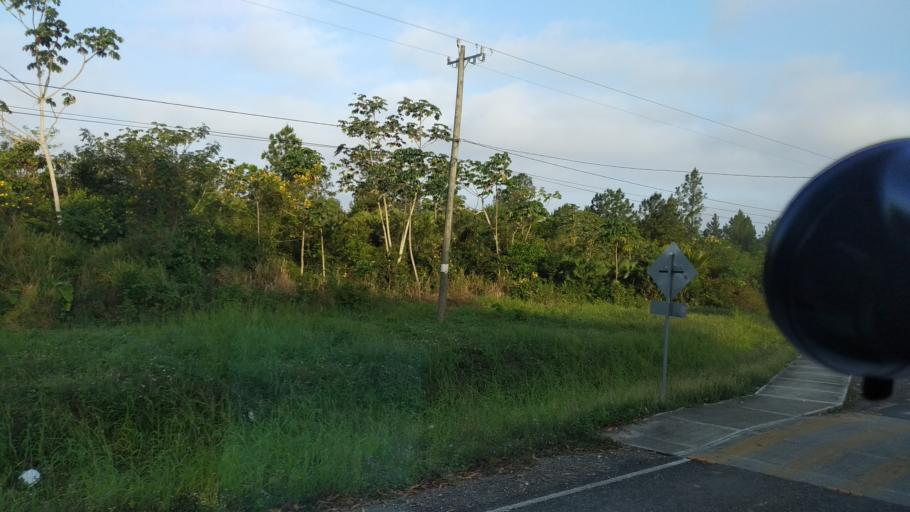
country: BZ
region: Stann Creek
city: Placencia
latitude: 16.5710
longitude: -88.5298
